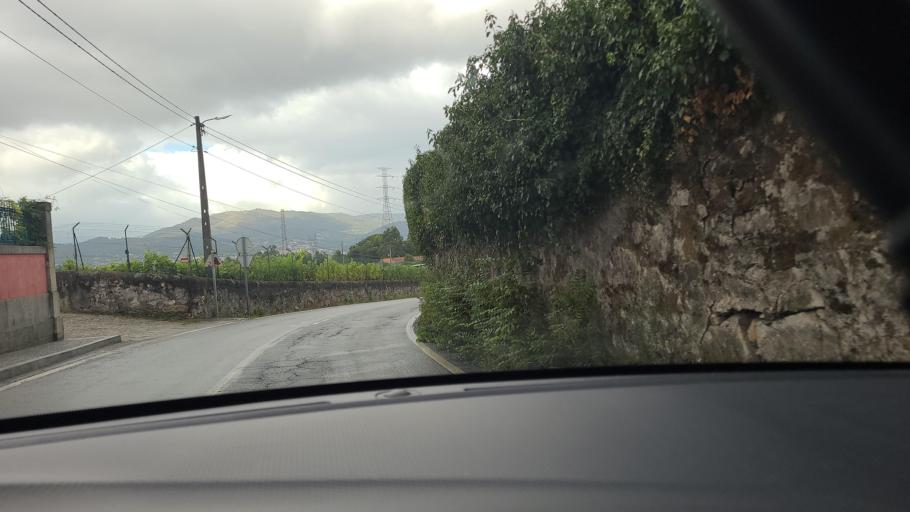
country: PT
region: Braga
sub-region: Braga
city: Adaufe
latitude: 41.5972
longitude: -8.3752
